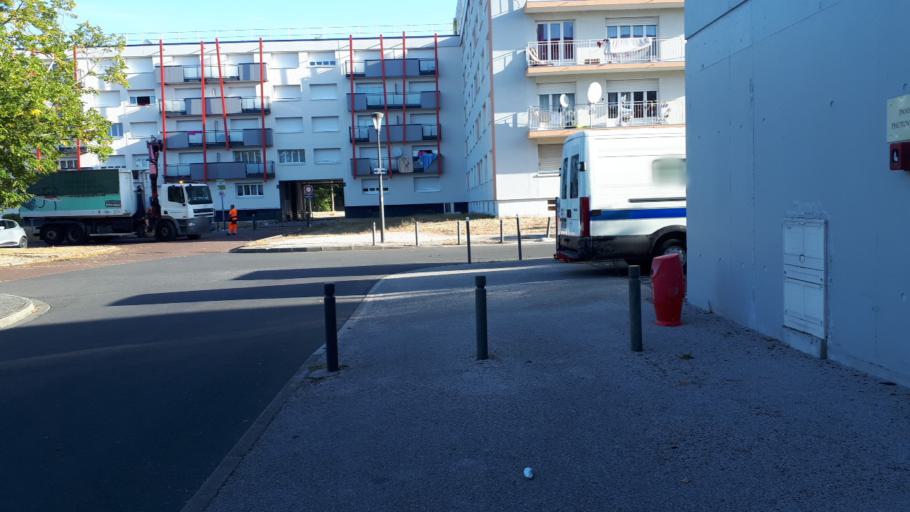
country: FR
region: Centre
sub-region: Departement du Loir-et-Cher
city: Blois
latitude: 47.5893
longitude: 1.3040
